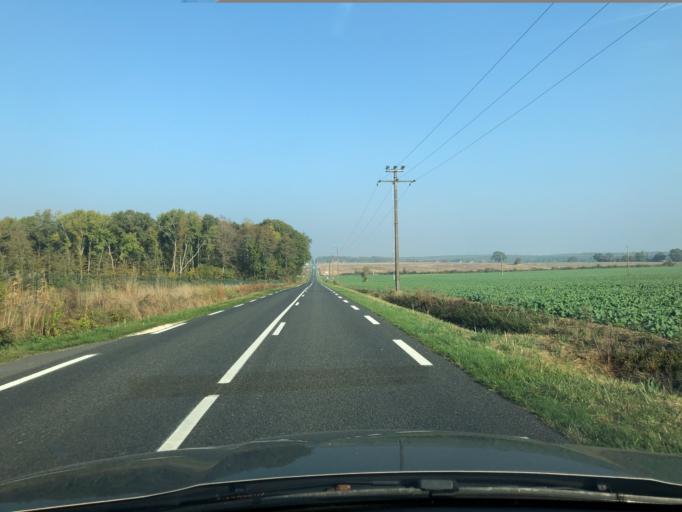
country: FR
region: Centre
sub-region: Departement d'Indre-et-Loire
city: Beaumont-la-Ronce
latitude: 47.6088
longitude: 0.6606
